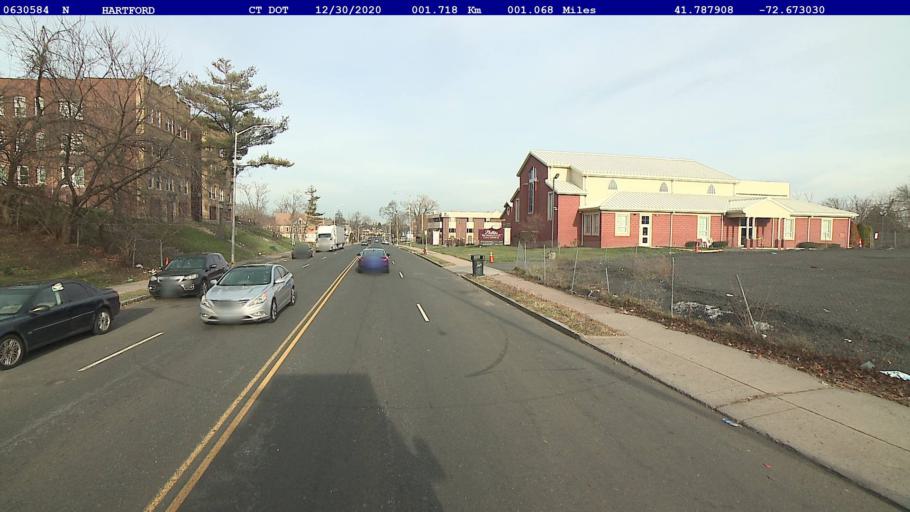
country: US
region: Connecticut
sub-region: Hartford County
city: Hartford
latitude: 41.7879
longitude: -72.6730
